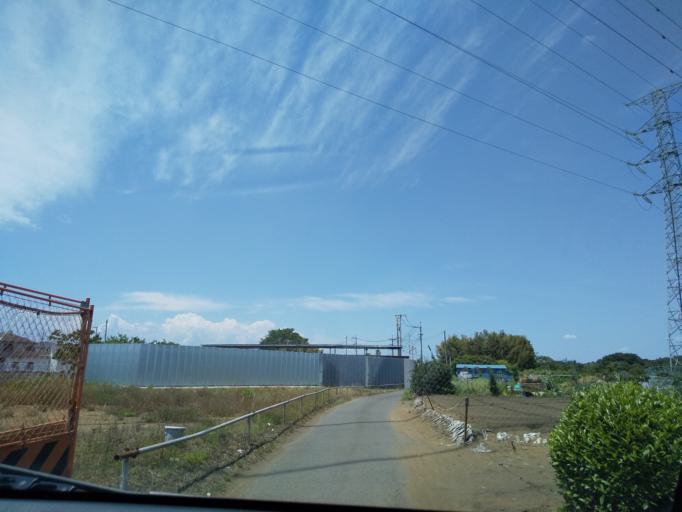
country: JP
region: Kanagawa
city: Zama
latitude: 35.5385
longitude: 139.3726
